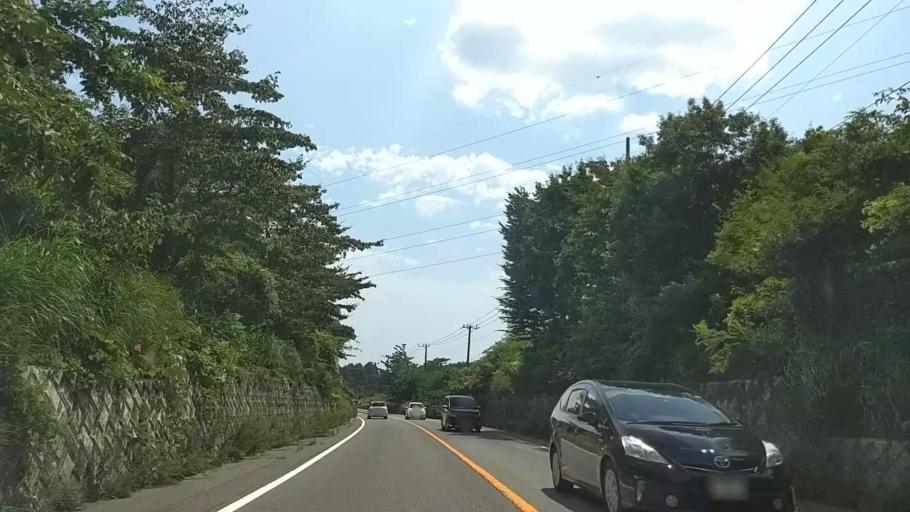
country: JP
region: Shizuoka
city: Fujinomiya
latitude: 35.3443
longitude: 138.5874
